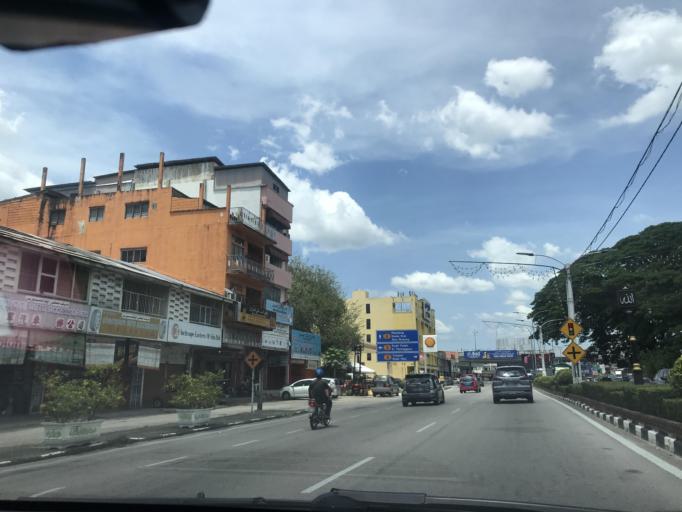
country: MY
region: Kelantan
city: Kota Bharu
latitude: 6.1192
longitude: 102.2413
